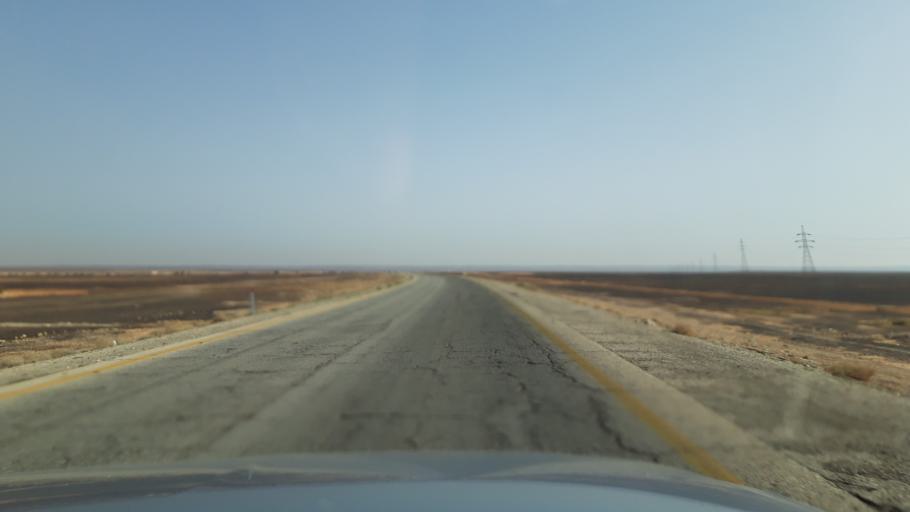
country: JO
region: Amman
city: Al Azraq ash Shamali
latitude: 31.7865
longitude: 36.5796
